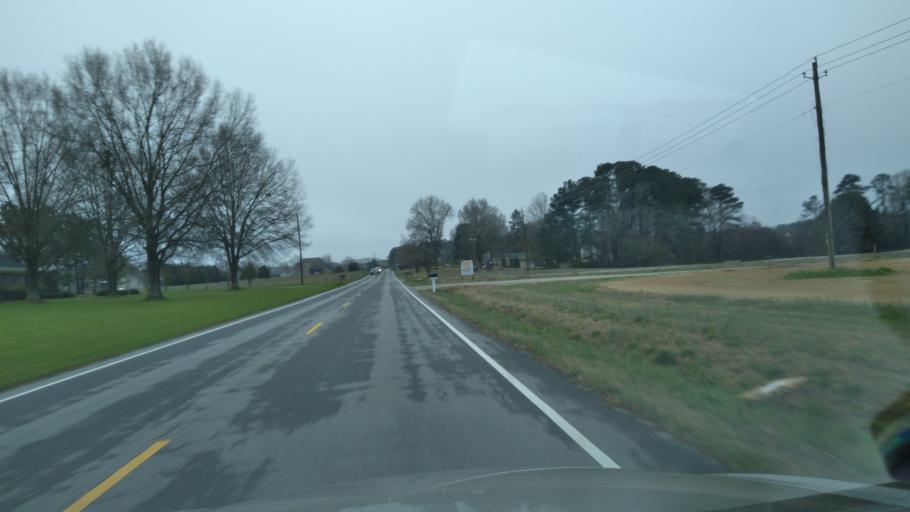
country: US
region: North Carolina
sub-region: Wake County
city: Knightdale
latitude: 35.7576
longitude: -78.4841
